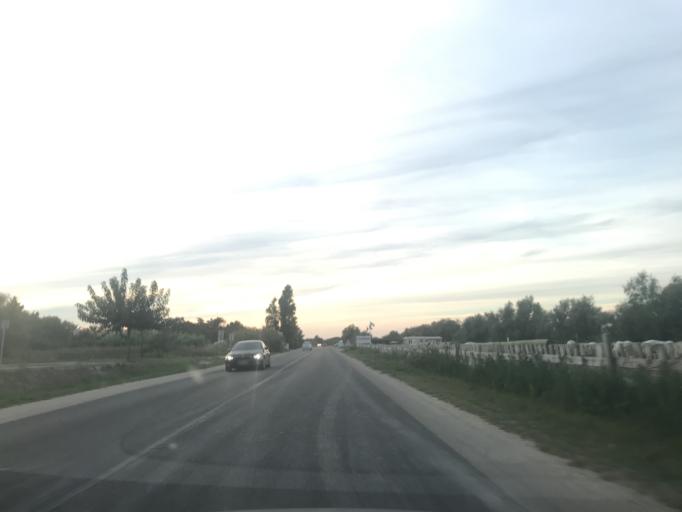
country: FR
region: Provence-Alpes-Cote d'Azur
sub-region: Departement des Bouches-du-Rhone
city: Saintes-Maries-de-la-Mer
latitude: 43.4588
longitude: 4.4253
